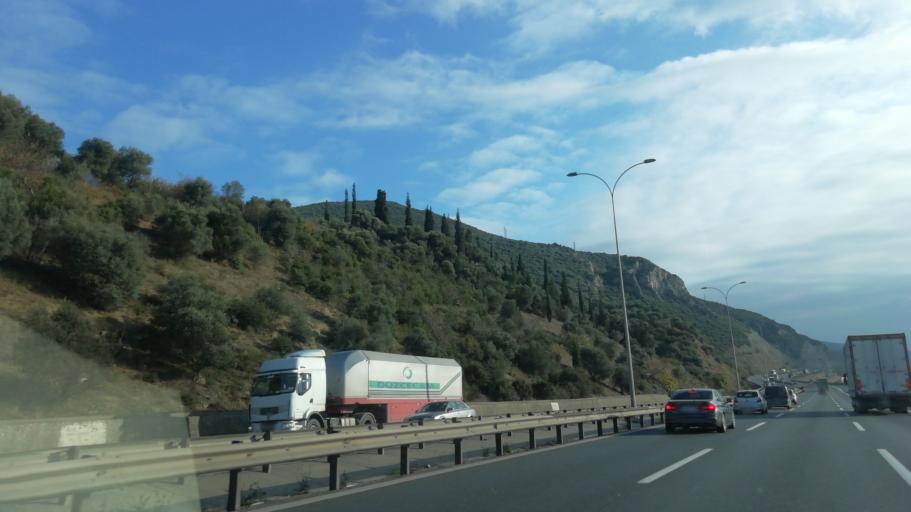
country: TR
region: Kocaeli
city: Hereke
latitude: 40.7773
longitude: 29.6405
